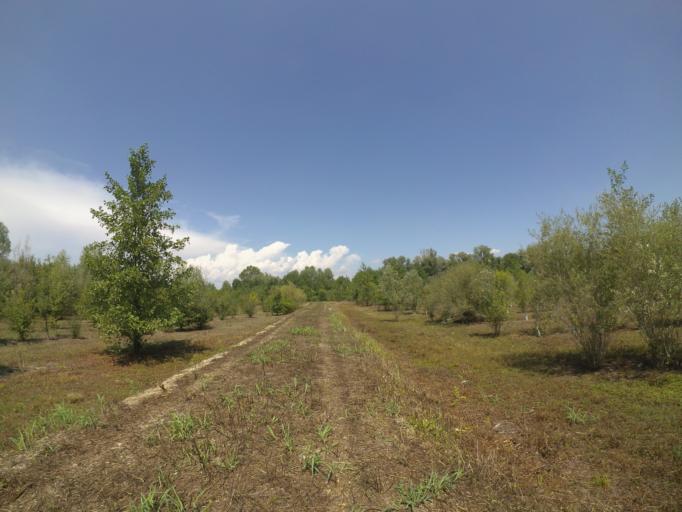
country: IT
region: Friuli Venezia Giulia
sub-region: Provincia di Udine
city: Rivignano
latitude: 45.8972
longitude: 13.0710
